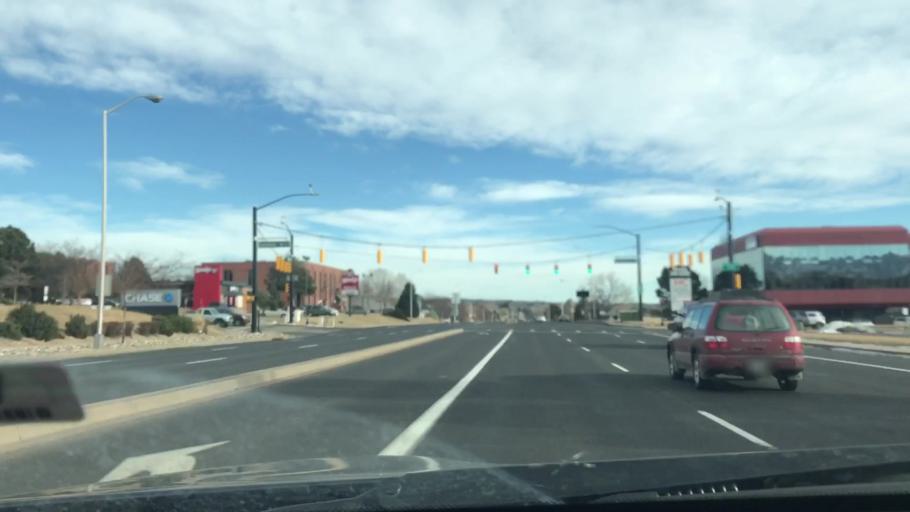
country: US
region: Colorado
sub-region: El Paso County
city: Colorado Springs
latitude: 38.9073
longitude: -104.7826
